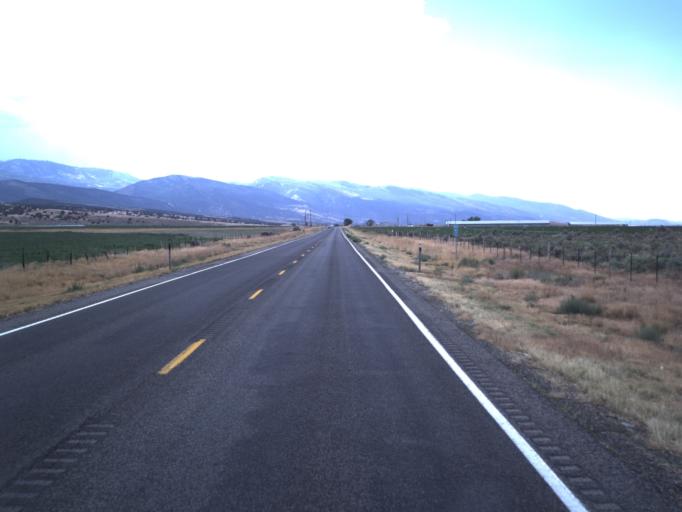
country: US
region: Utah
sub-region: Sanpete County
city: Ephraim
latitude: 39.4375
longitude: -111.5624
